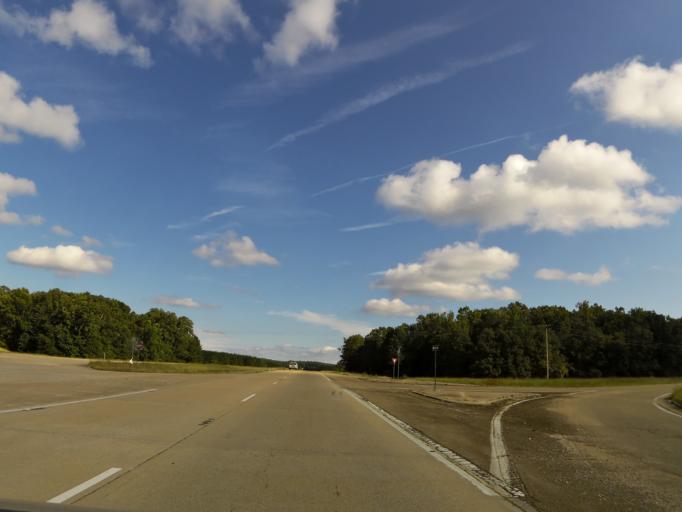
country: US
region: Mississippi
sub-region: Tishomingo County
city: Iuka
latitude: 34.8199
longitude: -88.2917
